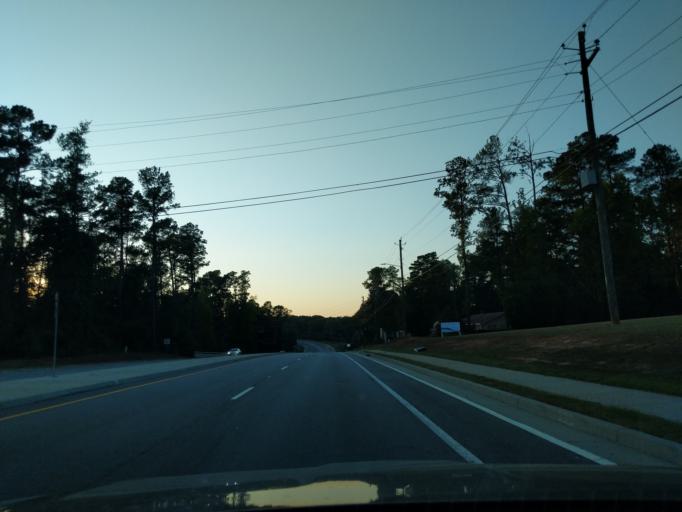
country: US
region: Georgia
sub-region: Columbia County
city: Martinez
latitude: 33.5227
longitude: -82.0888
